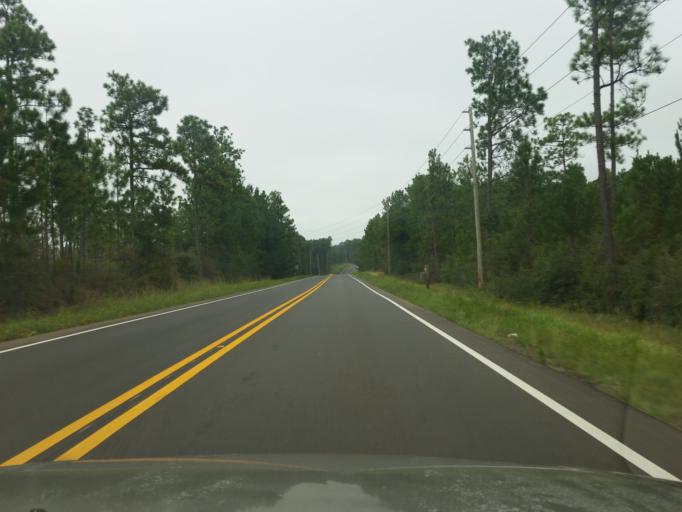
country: US
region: Alabama
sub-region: Baldwin County
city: Spanish Fort
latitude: 30.7901
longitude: -87.8762
